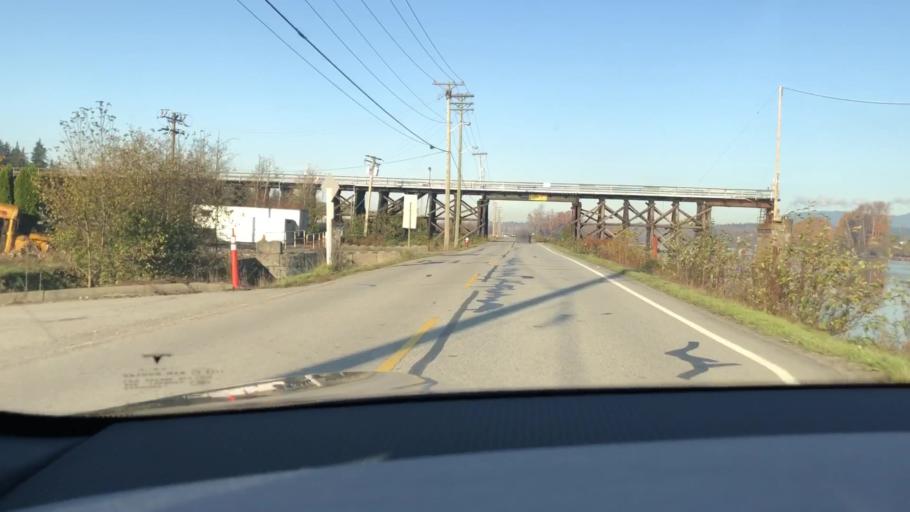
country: CA
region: British Columbia
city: New Westminster
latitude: 49.1818
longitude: -122.9875
